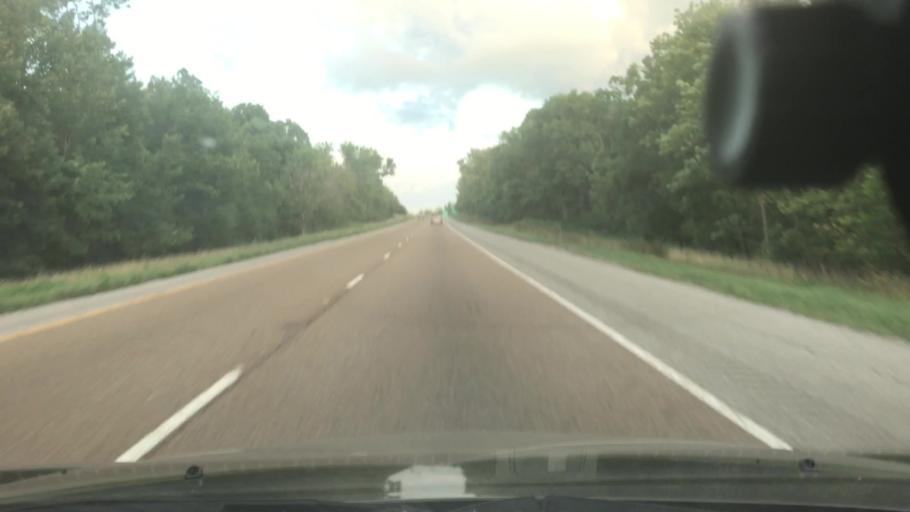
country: US
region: Illinois
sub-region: Saint Clair County
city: Scott Air Force Base
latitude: 38.5585
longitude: -89.8265
